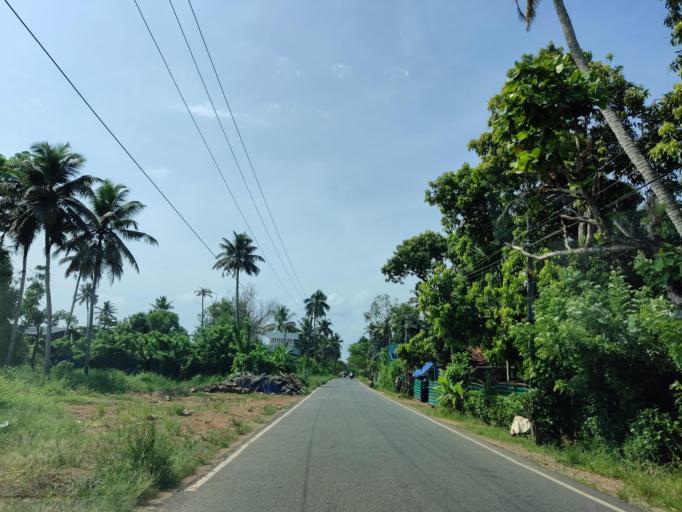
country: IN
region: Kerala
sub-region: Pattanamtitta
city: Tiruvalla
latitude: 9.3420
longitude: 76.4680
